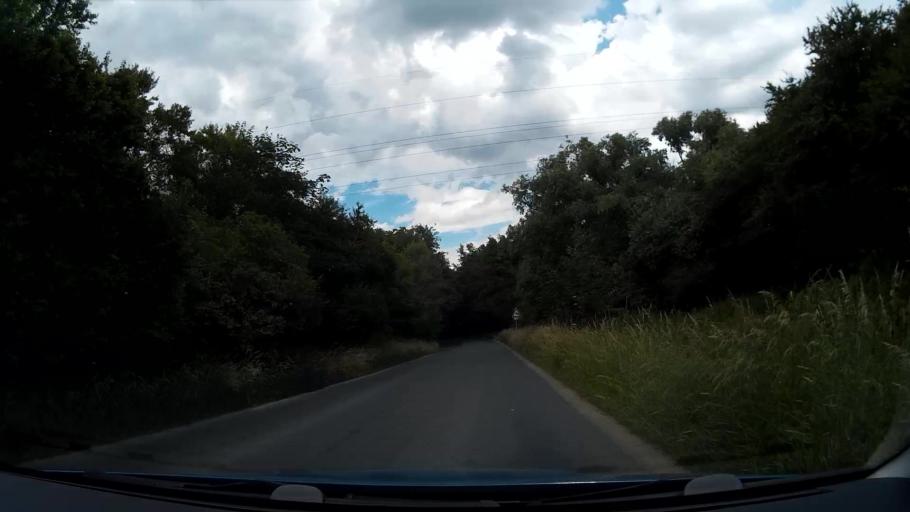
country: CZ
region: South Moravian
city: Orechov
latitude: 49.1214
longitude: 16.5263
